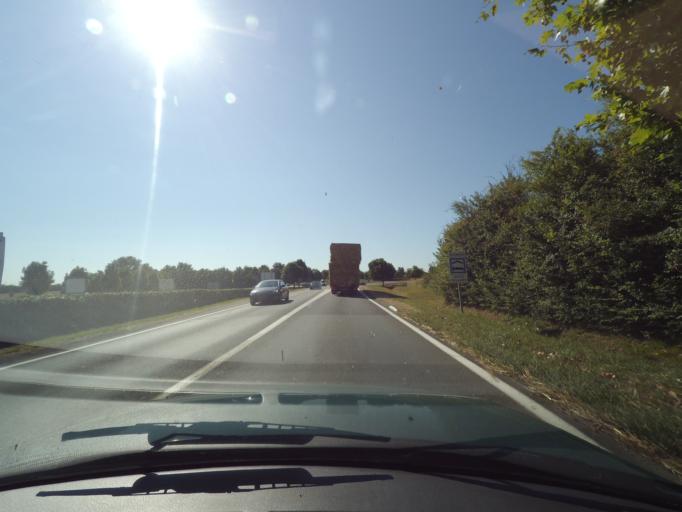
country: FR
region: Poitou-Charentes
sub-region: Departement de la Vienne
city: Lussac-les-Chateaux
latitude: 46.3970
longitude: 0.7312
